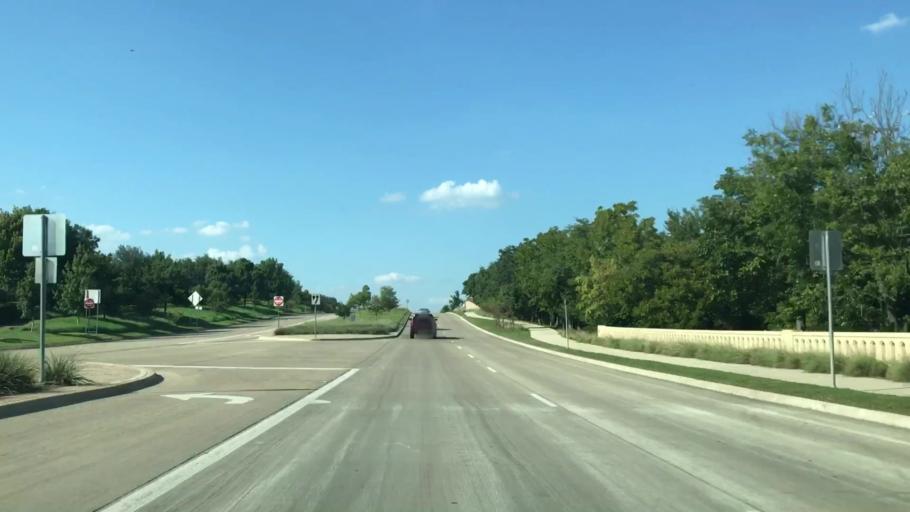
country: US
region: Texas
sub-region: Denton County
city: Trophy Club
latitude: 32.9650
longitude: -97.1858
